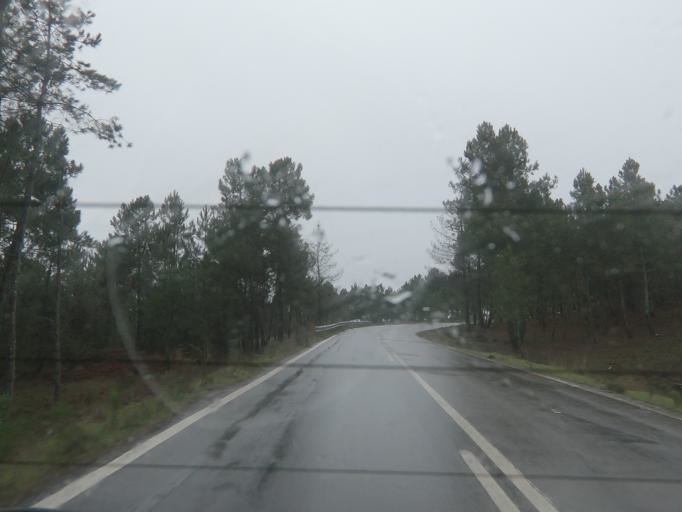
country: PT
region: Vila Real
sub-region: Sabrosa
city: Vilela
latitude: 41.2092
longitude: -7.6803
